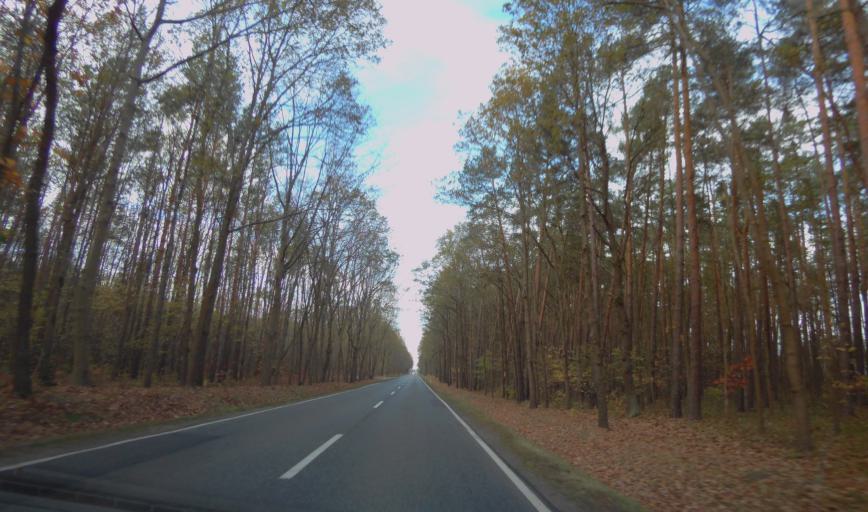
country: PL
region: Subcarpathian Voivodeship
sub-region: Powiat nizanski
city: Krzeszow
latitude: 50.3919
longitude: 22.3021
